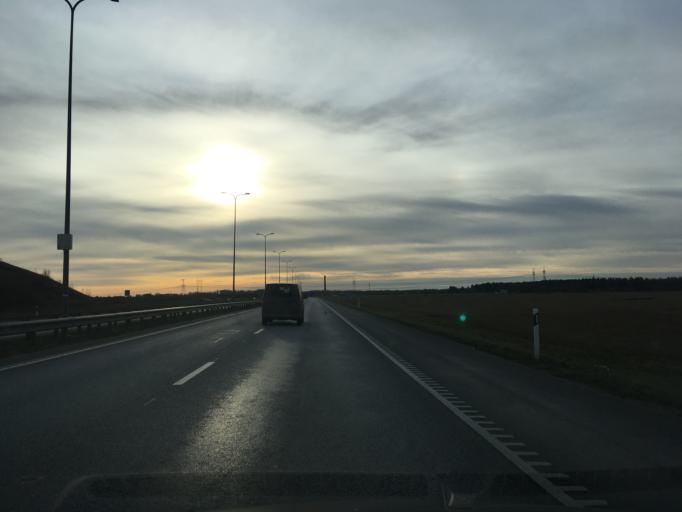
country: EE
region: Ida-Virumaa
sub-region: Kohtla-Jaerve linn
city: Kohtla-Jarve
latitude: 59.3962
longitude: 27.3344
